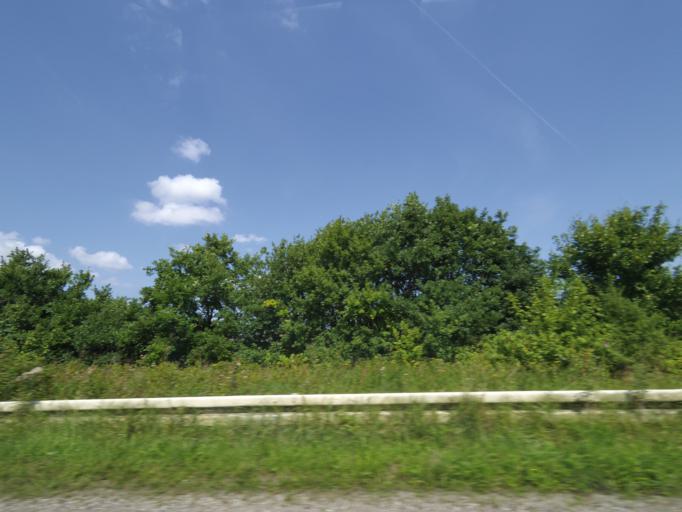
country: DK
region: South Denmark
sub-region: Assens Kommune
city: Arup
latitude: 55.4086
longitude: 10.0547
